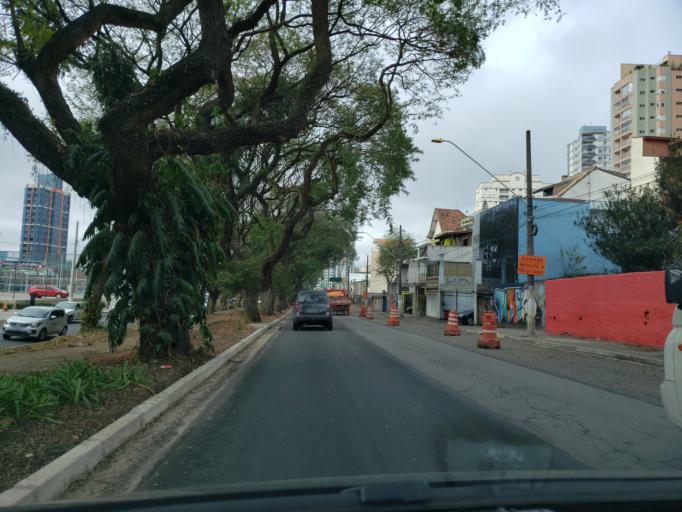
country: BR
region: Sao Paulo
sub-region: Santo Andre
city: Santo Andre
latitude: -23.6449
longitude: -46.5417
